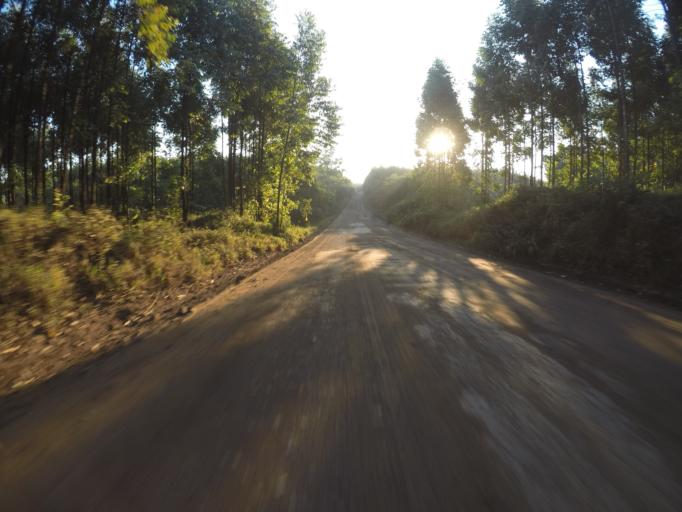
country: ZA
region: KwaZulu-Natal
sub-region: uThungulu District Municipality
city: KwaMbonambi
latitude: -28.6765
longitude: 32.1170
